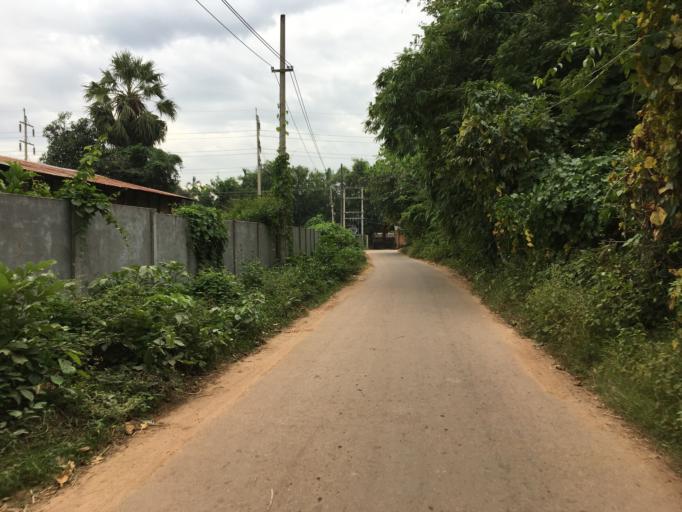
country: MM
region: Mon
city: Mawlamyine
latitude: 16.4291
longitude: 97.6285
